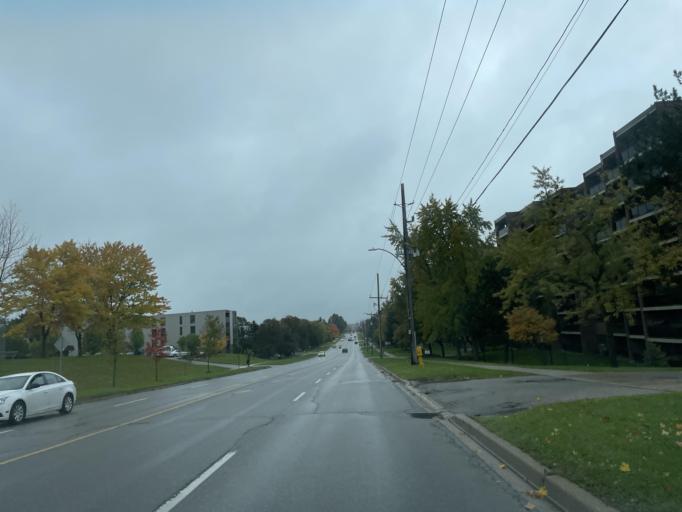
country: CA
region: Ontario
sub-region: Wellington County
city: Guelph
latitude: 43.5380
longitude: -80.2777
